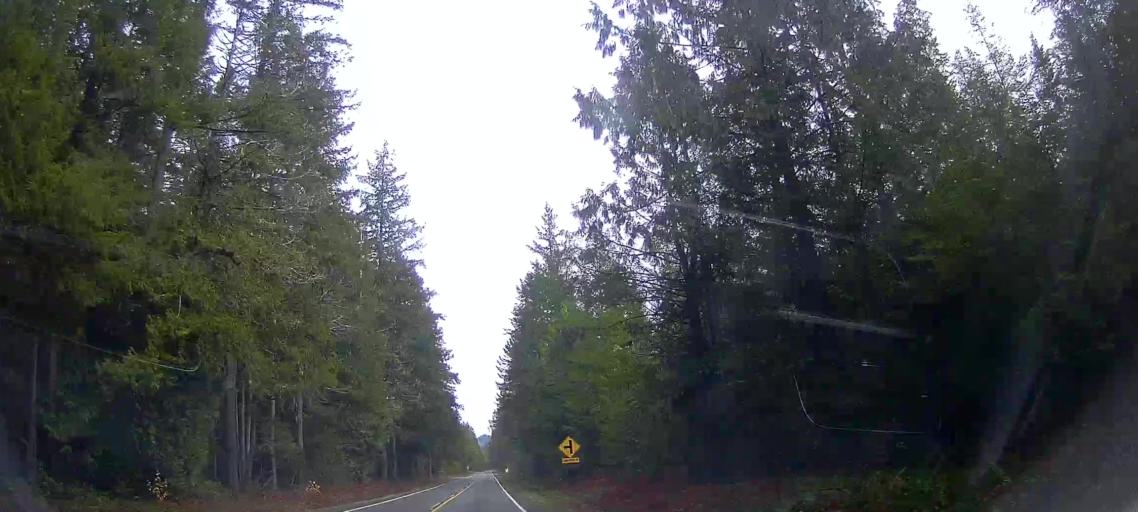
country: US
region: Washington
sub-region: Snohomish County
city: Darrington
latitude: 48.5273
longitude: -121.8280
